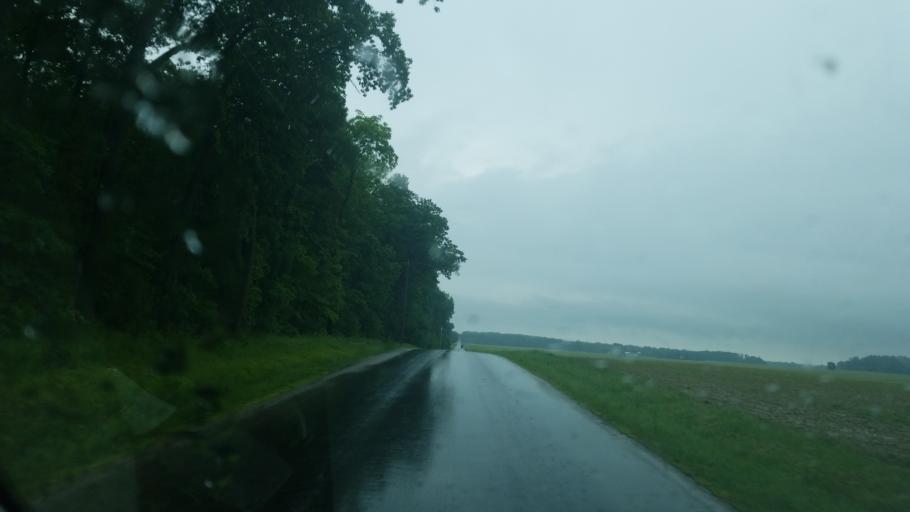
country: US
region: Ohio
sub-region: Huron County
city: Plymouth
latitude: 40.9449
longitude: -82.7033
